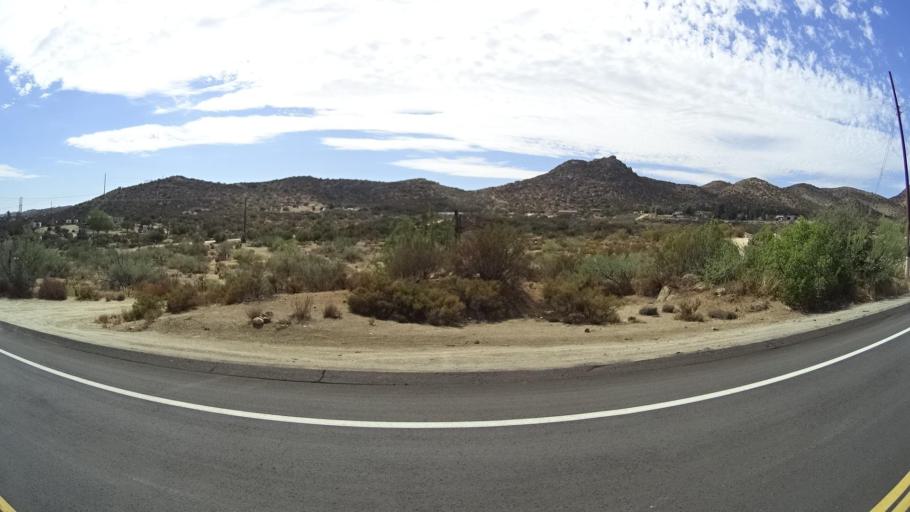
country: MX
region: Baja California
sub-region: Tecate
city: Cereso del Hongo
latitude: 32.6259
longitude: -116.2219
